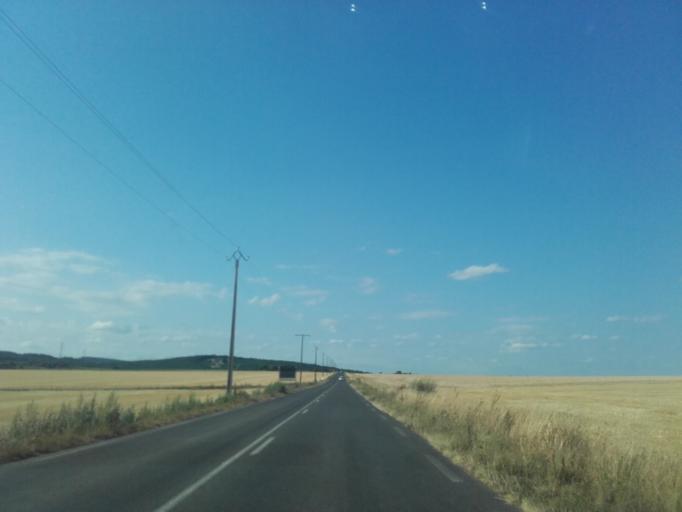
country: FR
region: Bourgogne
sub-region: Departement de Saone-et-Loire
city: Mellecey
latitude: 46.8229
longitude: 4.7521
